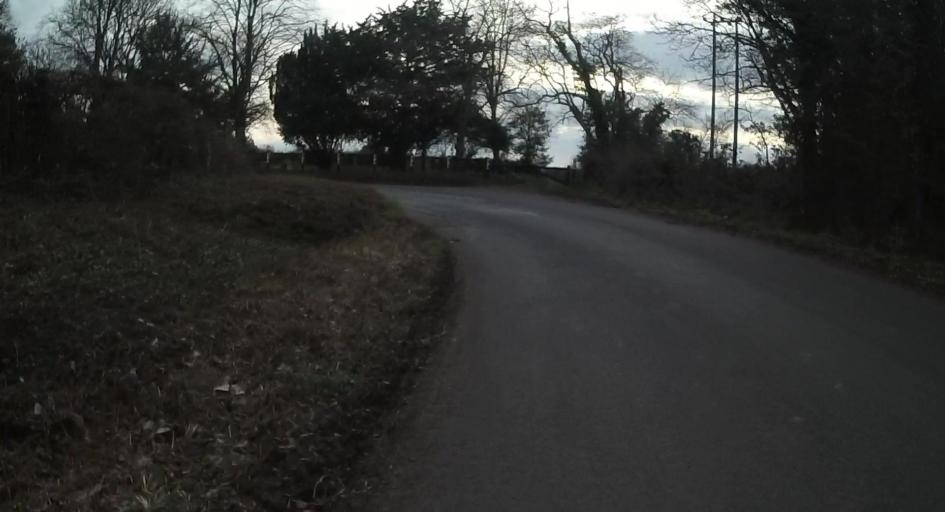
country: GB
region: England
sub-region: West Berkshire
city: Theale
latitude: 51.4076
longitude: -1.0742
